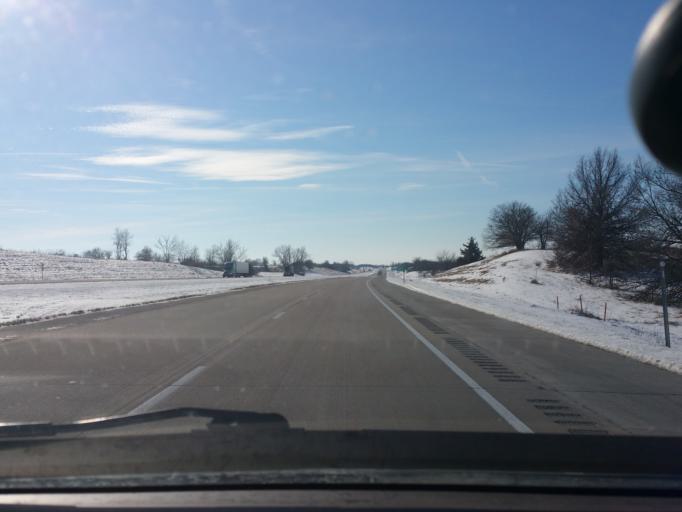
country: US
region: Iowa
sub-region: Decatur County
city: Leon
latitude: 40.7566
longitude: -93.8374
